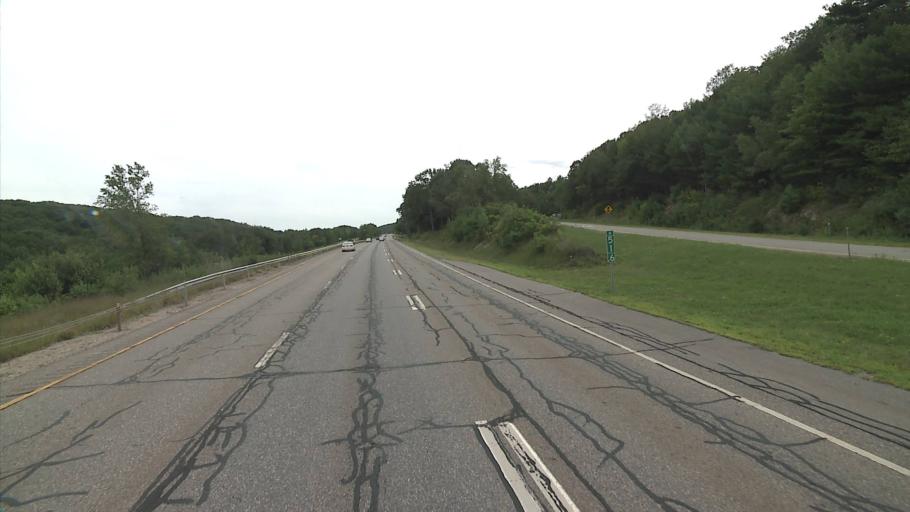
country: US
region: Connecticut
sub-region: Litchfield County
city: Torrington
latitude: 41.8284
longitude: -73.1068
